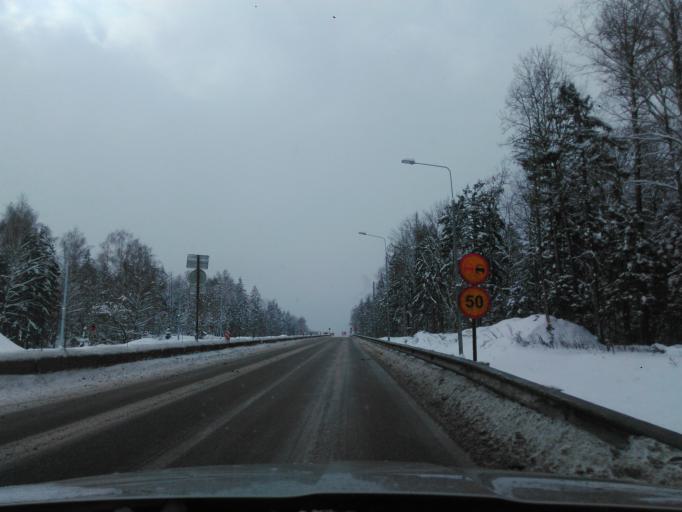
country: RU
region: Moskovskaya
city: Povarovo
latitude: 56.0275
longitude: 37.0551
